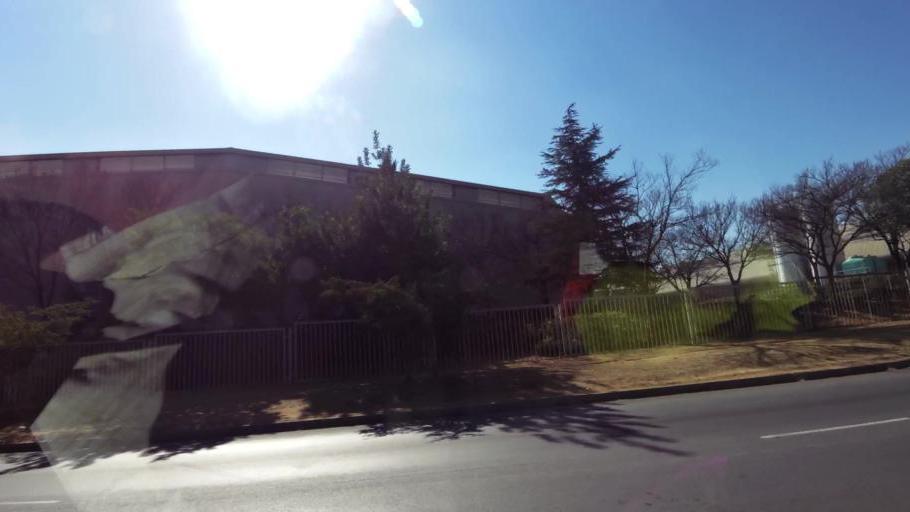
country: ZA
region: Gauteng
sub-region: City of Johannesburg Metropolitan Municipality
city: Johannesburg
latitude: -26.2517
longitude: 27.9728
